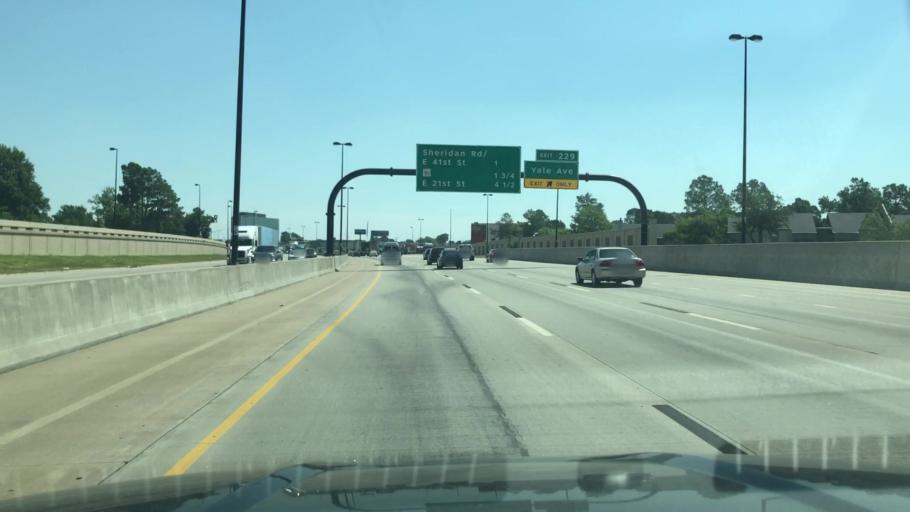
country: US
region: Oklahoma
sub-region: Tulsa County
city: Jenks
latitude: 36.0918
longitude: -95.9289
